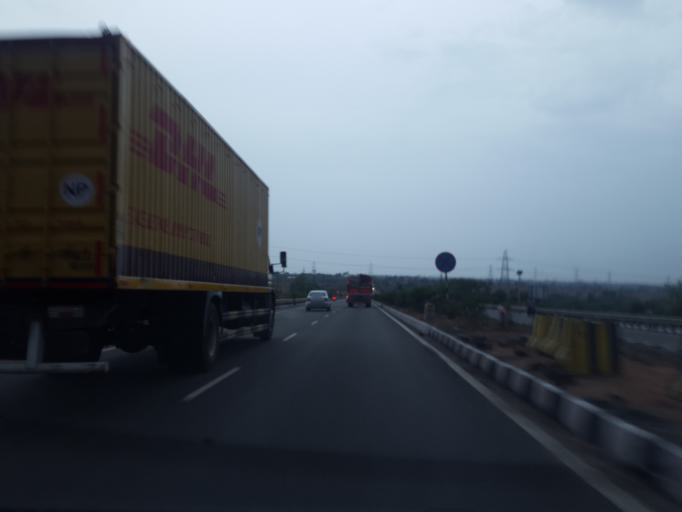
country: IN
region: Telangana
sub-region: Mahbubnagar
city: Farrukhnagar
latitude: 17.0981
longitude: 78.2484
